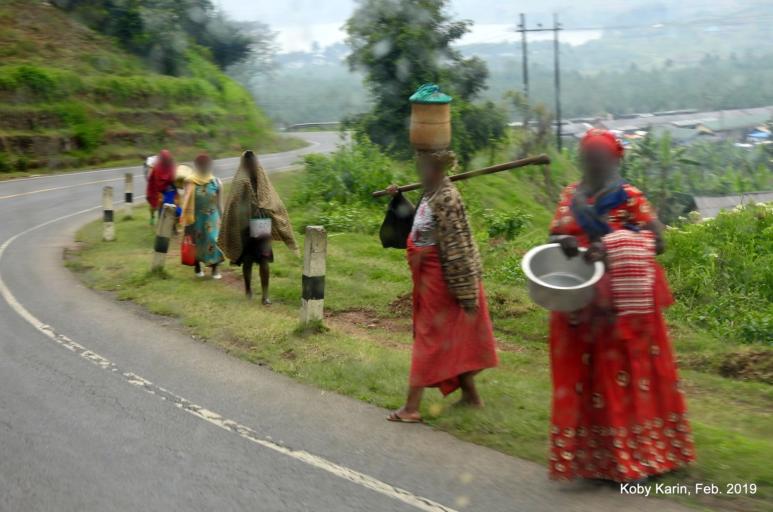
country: UG
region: Western Region
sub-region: Kisoro District
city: Kisoro
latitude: -1.2064
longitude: 29.8187
